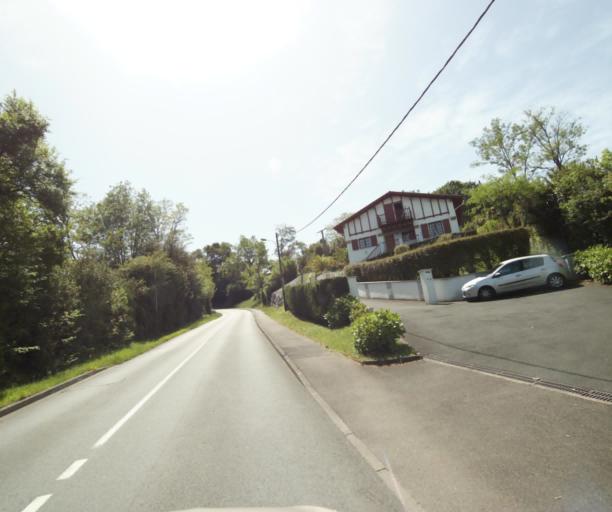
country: FR
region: Aquitaine
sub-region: Departement des Pyrenees-Atlantiques
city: Mouguerre
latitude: 43.4602
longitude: -1.4401
